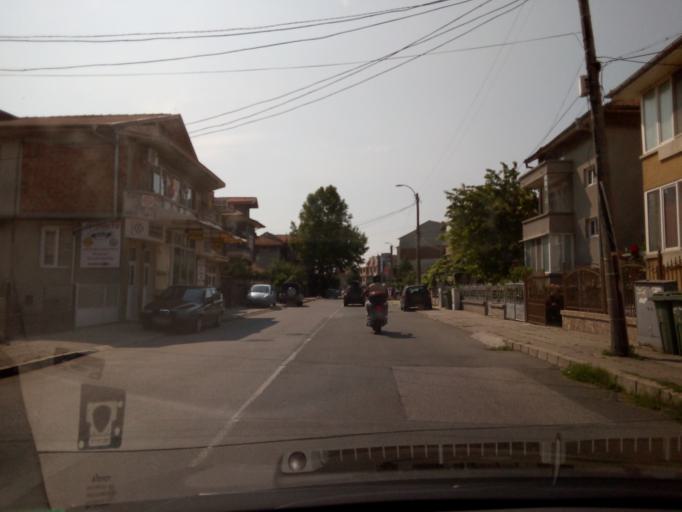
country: BG
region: Burgas
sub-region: Obshtina Pomorie
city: Pomorie
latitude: 42.5711
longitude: 27.6128
